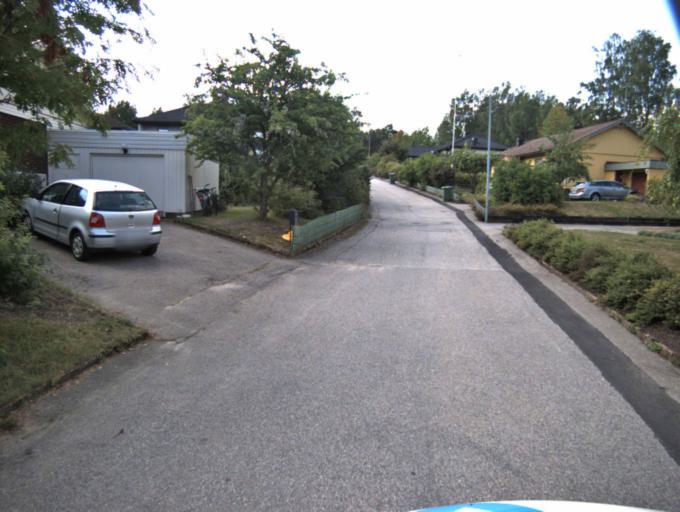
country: SE
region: Vaestra Goetaland
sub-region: Ulricehamns Kommun
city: Ulricehamn
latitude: 57.6831
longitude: 13.3765
